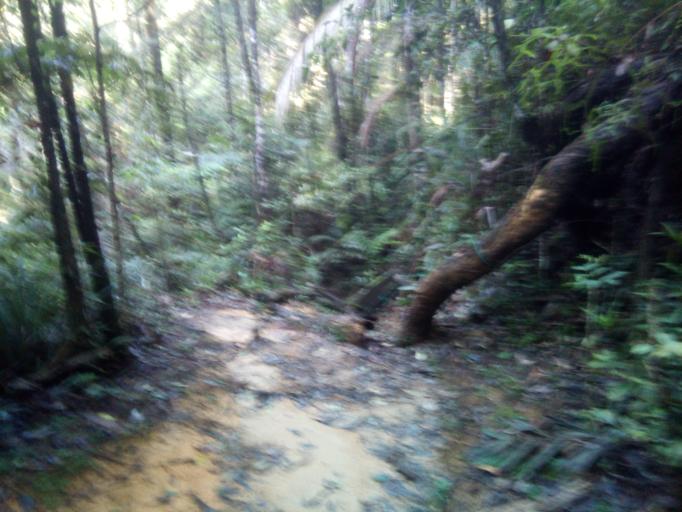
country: MY
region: Penang
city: Tanjung Tokong
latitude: 5.4176
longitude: 100.2581
